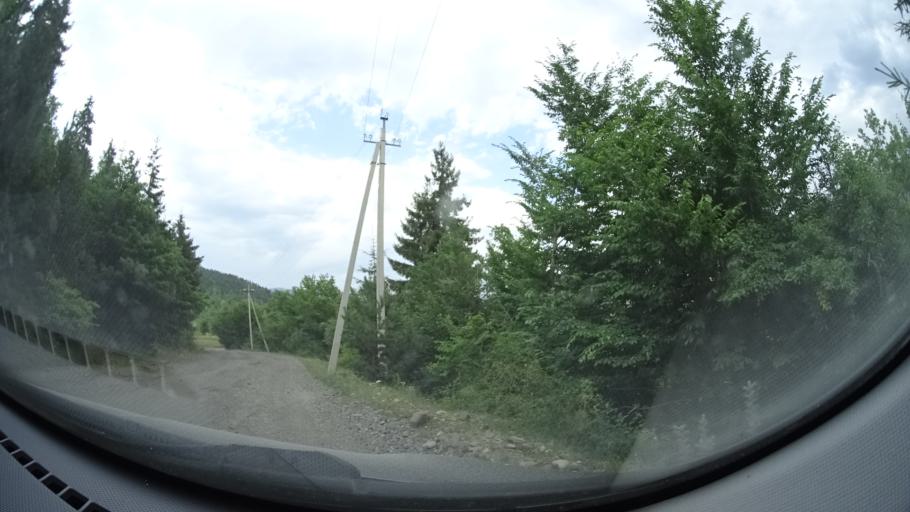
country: GE
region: Samtskhe-Javakheti
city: Adigeni
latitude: 41.6664
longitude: 42.6205
